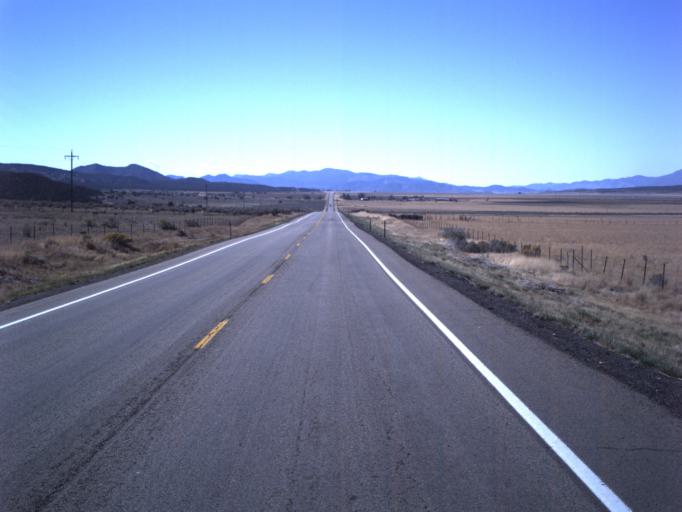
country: US
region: Utah
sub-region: Juab County
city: Nephi
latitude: 39.4978
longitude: -111.8778
